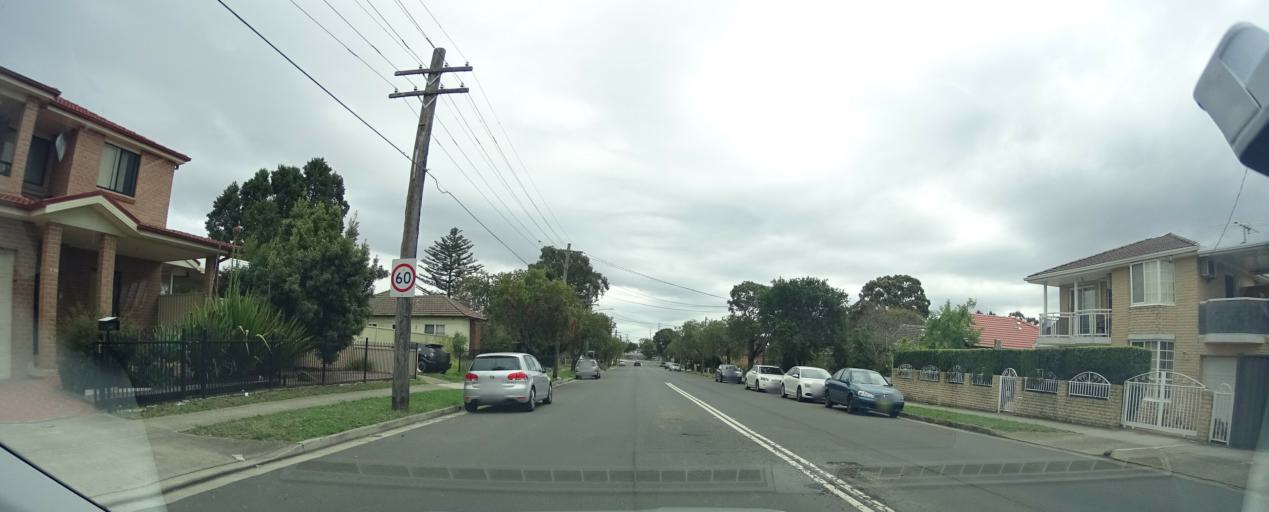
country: AU
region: New South Wales
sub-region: Bankstown
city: Padstow
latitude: -33.9538
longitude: 151.0282
